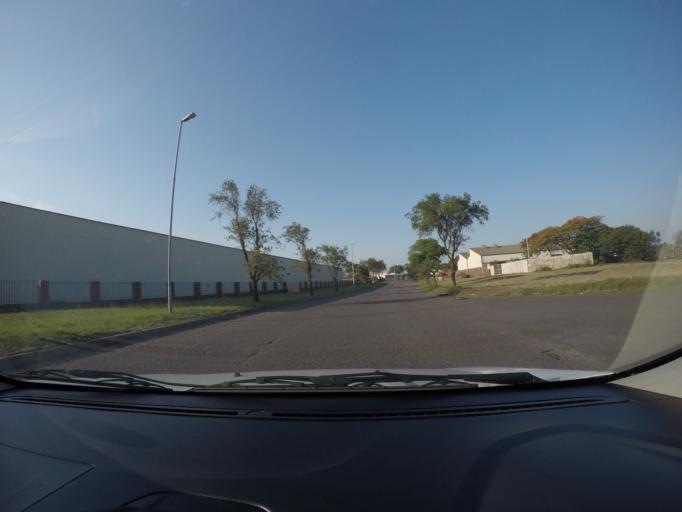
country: ZA
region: KwaZulu-Natal
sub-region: uThungulu District Municipality
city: Richards Bay
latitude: -28.7639
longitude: 32.0044
